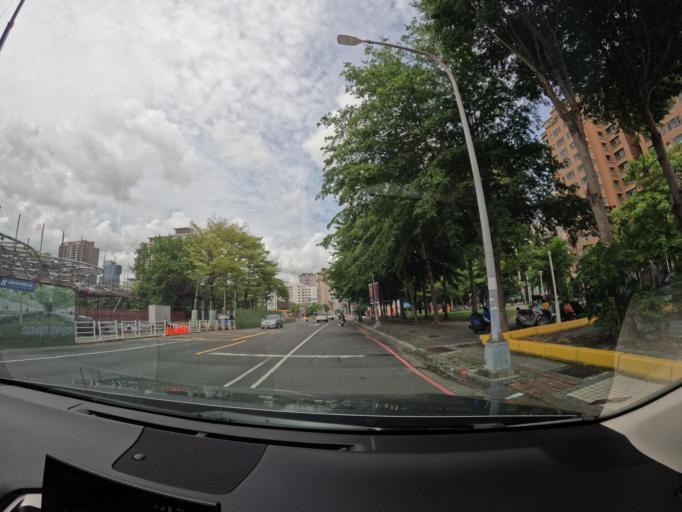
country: TW
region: Kaohsiung
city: Kaohsiung
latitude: 22.6548
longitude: 120.2872
